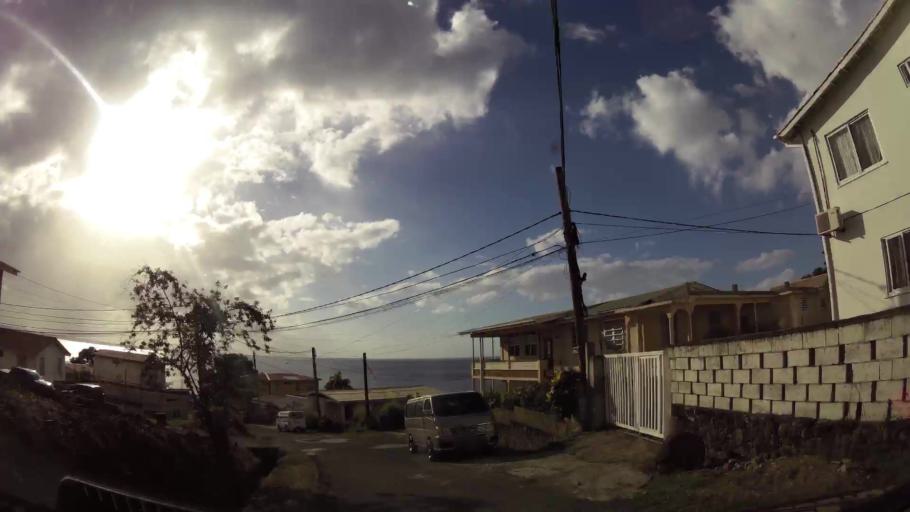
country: DM
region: Saint Paul
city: Mahaut
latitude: 15.3409
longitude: -61.3904
